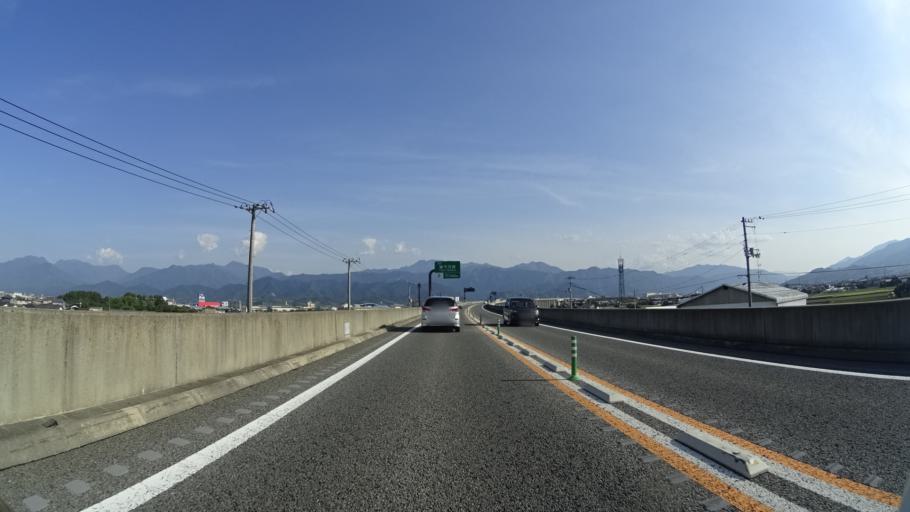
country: JP
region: Ehime
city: Saijo
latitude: 33.9255
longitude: 133.0744
